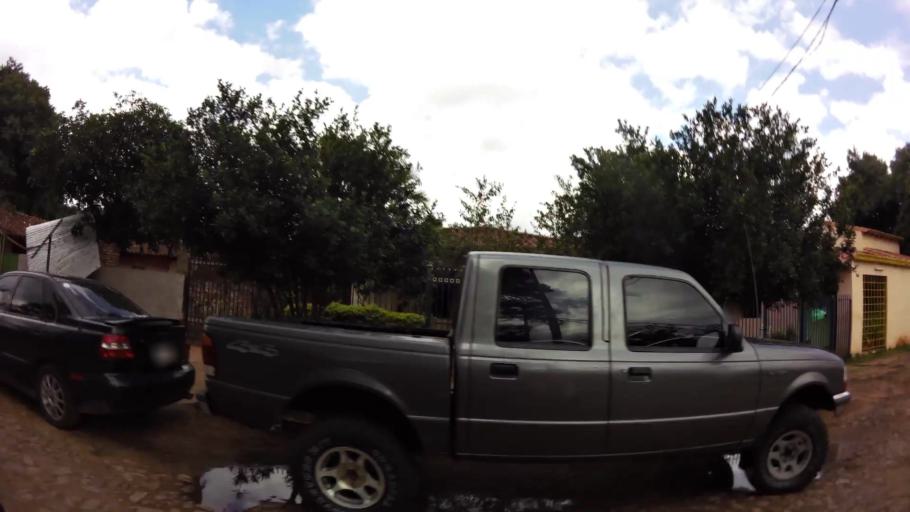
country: PY
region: Central
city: San Lorenzo
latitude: -25.2774
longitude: -57.4886
